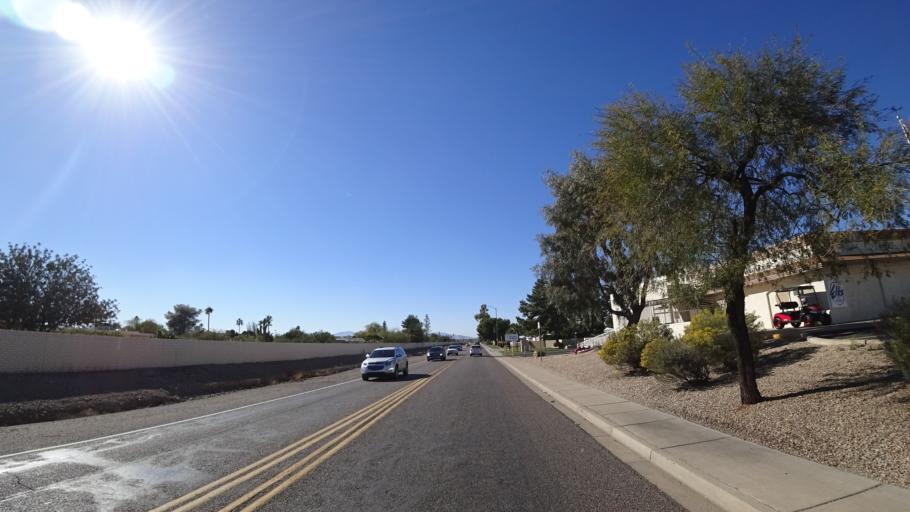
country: US
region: Arizona
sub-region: Maricopa County
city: Surprise
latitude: 33.6526
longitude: -112.2916
